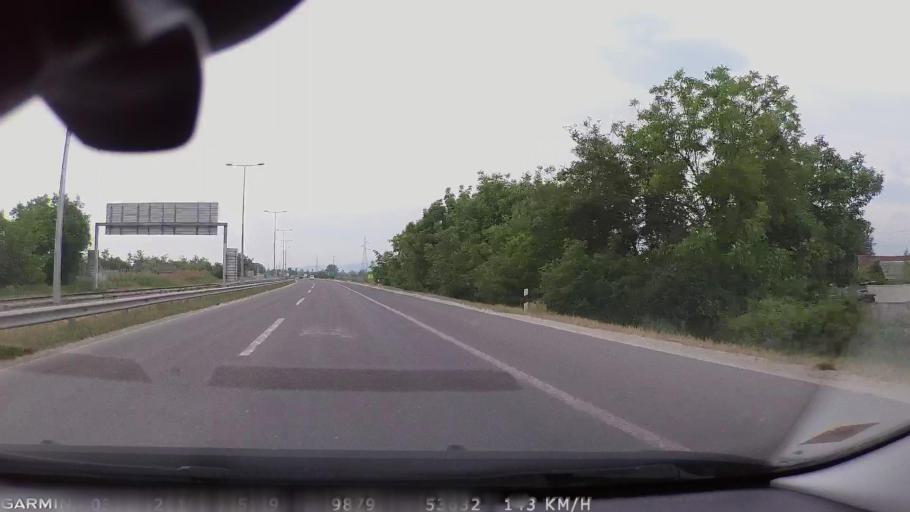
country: MK
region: Ilinden
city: Jurumleri
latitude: 41.9861
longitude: 21.5371
